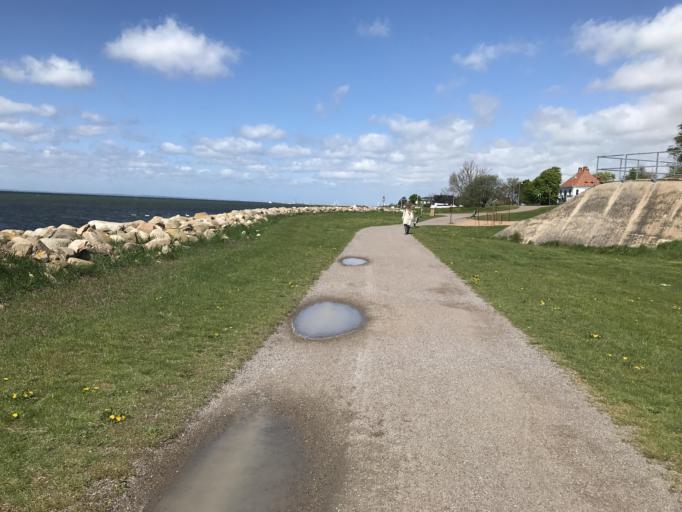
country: SE
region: Skane
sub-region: Landskrona
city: Landskrona
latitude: 55.8836
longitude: 12.8125
